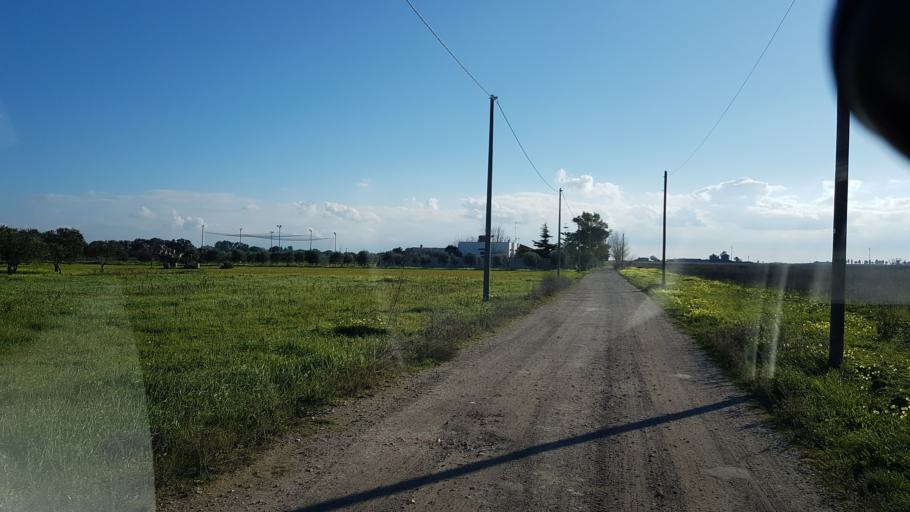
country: IT
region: Apulia
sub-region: Provincia di Brindisi
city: Tuturano
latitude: 40.5432
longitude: 17.9587
